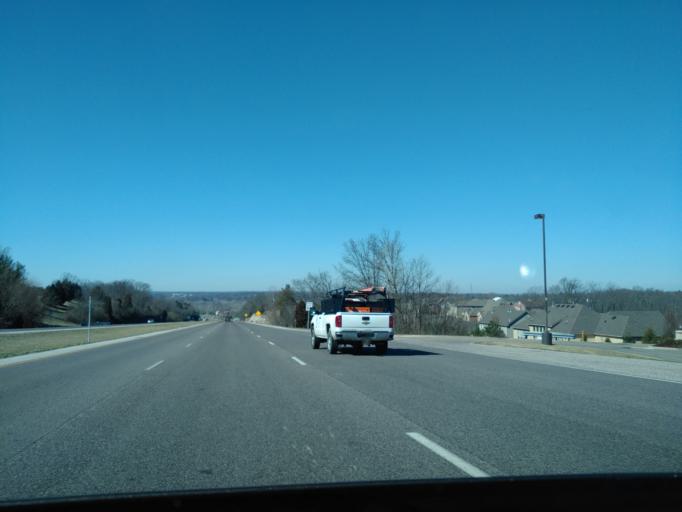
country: US
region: Missouri
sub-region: Saint Louis County
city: Sunset Hills
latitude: 38.5246
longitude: -90.4026
